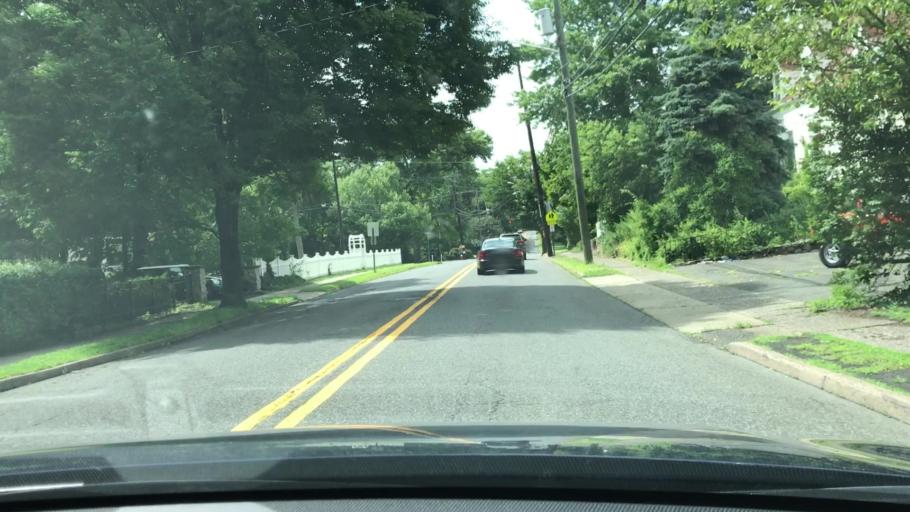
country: US
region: New Jersey
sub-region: Bergen County
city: Ridgewood
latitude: 40.9788
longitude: -74.1272
